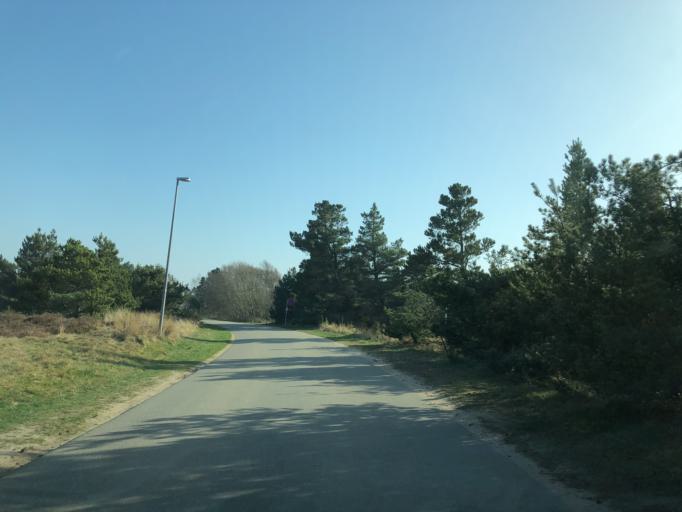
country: DK
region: South Denmark
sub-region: Varde Kommune
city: Oksbol
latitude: 55.5600
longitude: 8.1334
